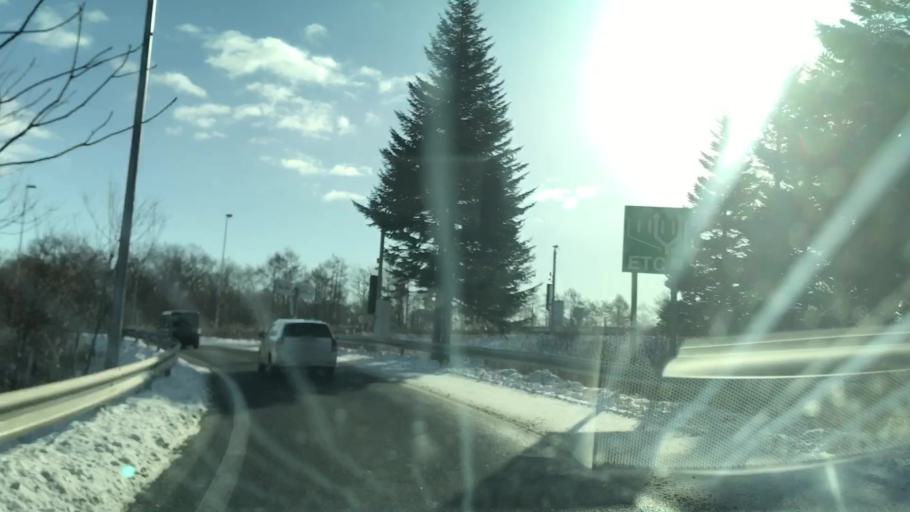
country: JP
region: Hokkaido
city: Chitose
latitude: 42.8125
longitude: 141.6213
